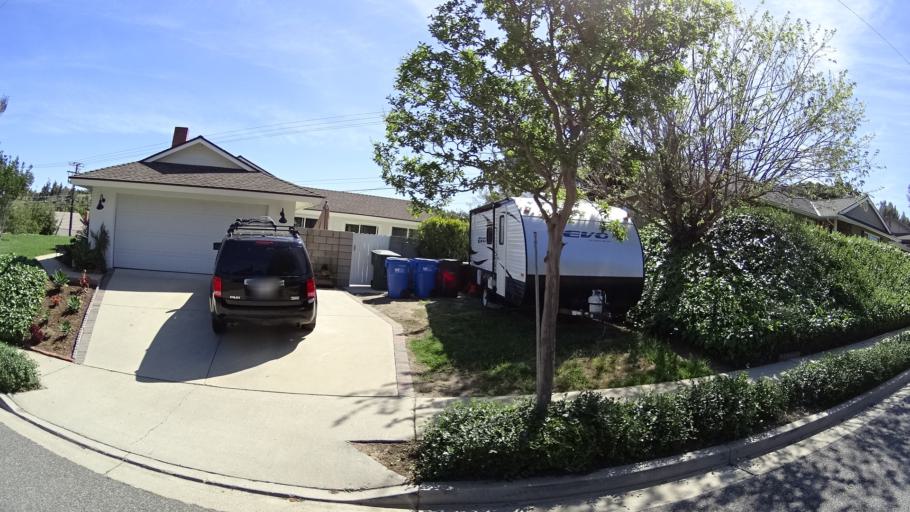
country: US
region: California
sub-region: Ventura County
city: Thousand Oaks
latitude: 34.2225
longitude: -118.8606
